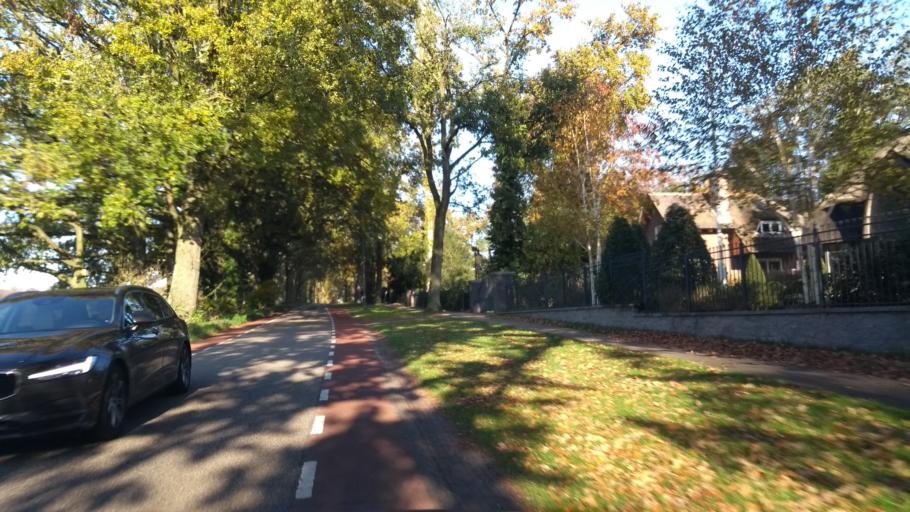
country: NL
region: Gelderland
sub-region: Gemeente Rheden
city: Rheden
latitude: 52.0122
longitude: 6.0304
